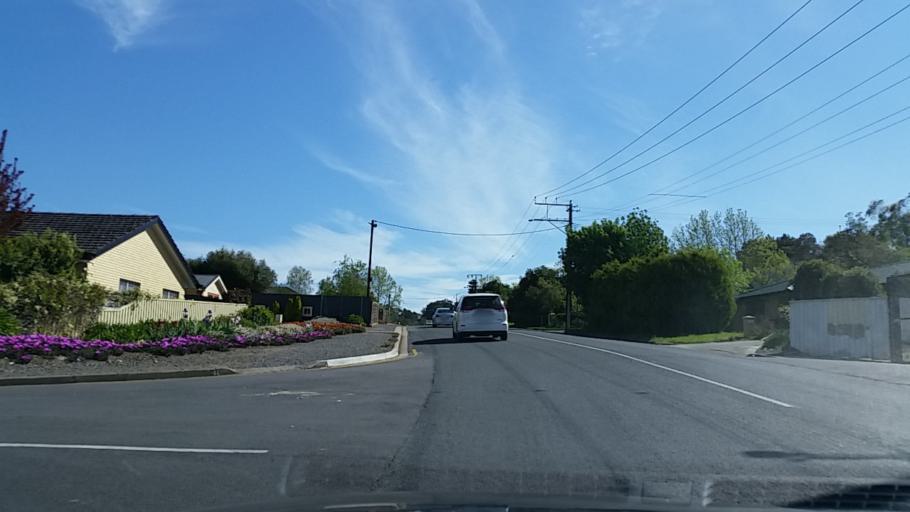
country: AU
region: South Australia
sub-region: Mount Barker
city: Mount Barker
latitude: -35.0642
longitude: 138.8529
